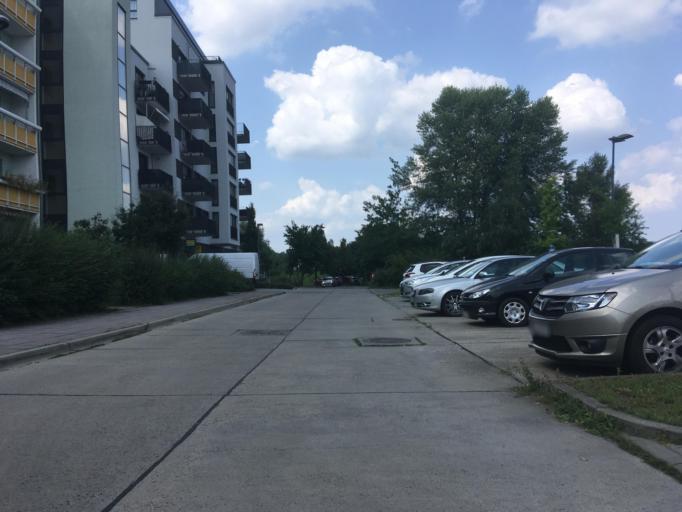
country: DE
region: Brandenburg
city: Wildau
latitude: 52.3251
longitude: 13.6231
